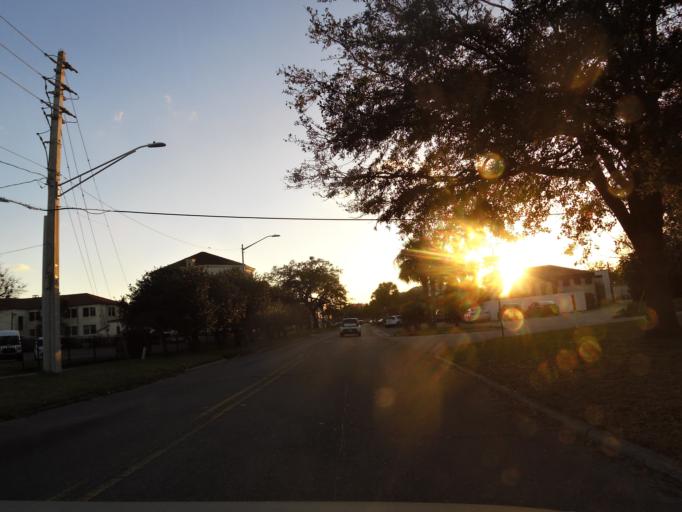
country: US
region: Florida
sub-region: Duval County
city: Jacksonville
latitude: 30.3114
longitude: -81.6924
